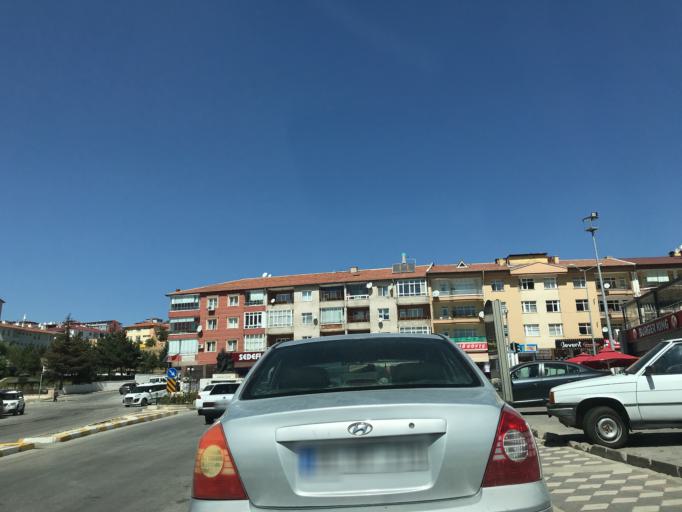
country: TR
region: Yozgat
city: Yozgat
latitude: 39.8242
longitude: 34.8181
